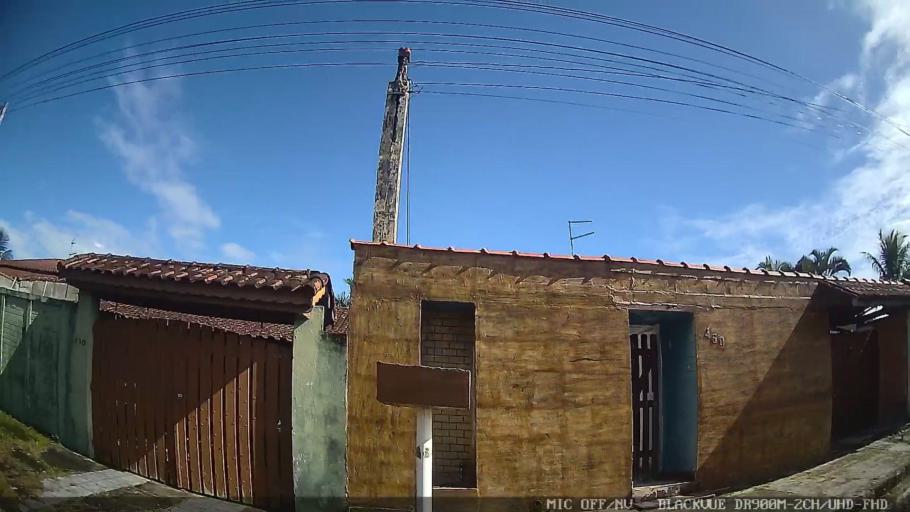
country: BR
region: Sao Paulo
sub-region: Itanhaem
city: Itanhaem
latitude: -24.2399
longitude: -46.8976
